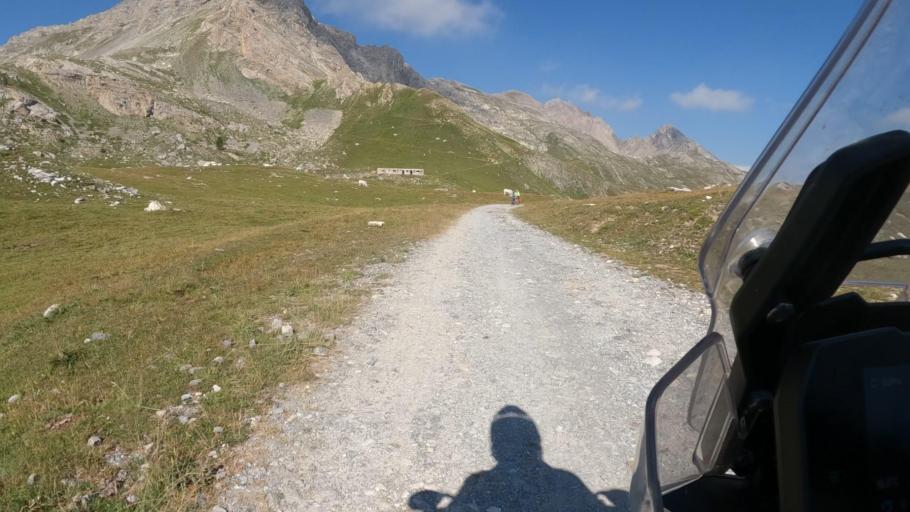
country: IT
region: Piedmont
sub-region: Provincia di Cuneo
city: Bersezio
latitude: 44.3990
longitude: 7.0203
